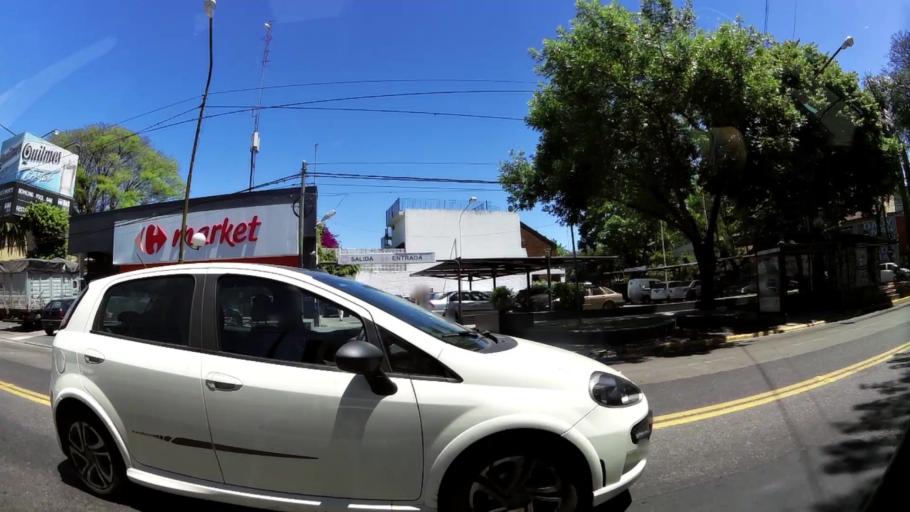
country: AR
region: Buenos Aires
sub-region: Partido de Vicente Lopez
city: Olivos
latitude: -34.4902
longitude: -58.4848
